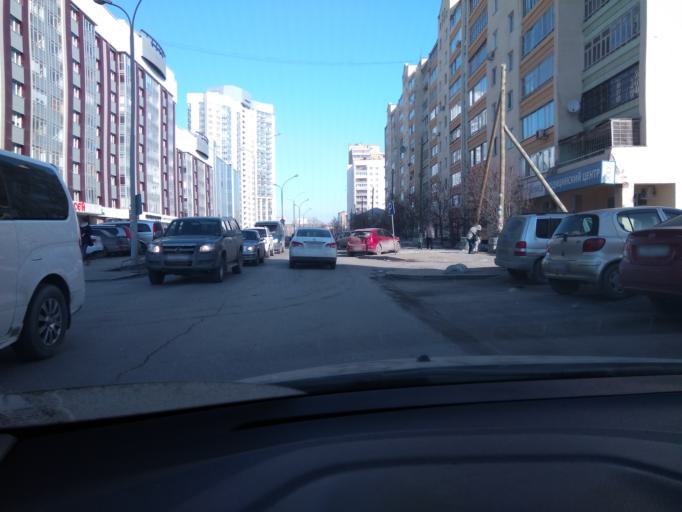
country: RU
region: Sverdlovsk
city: Yekaterinburg
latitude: 56.8426
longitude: 60.5734
